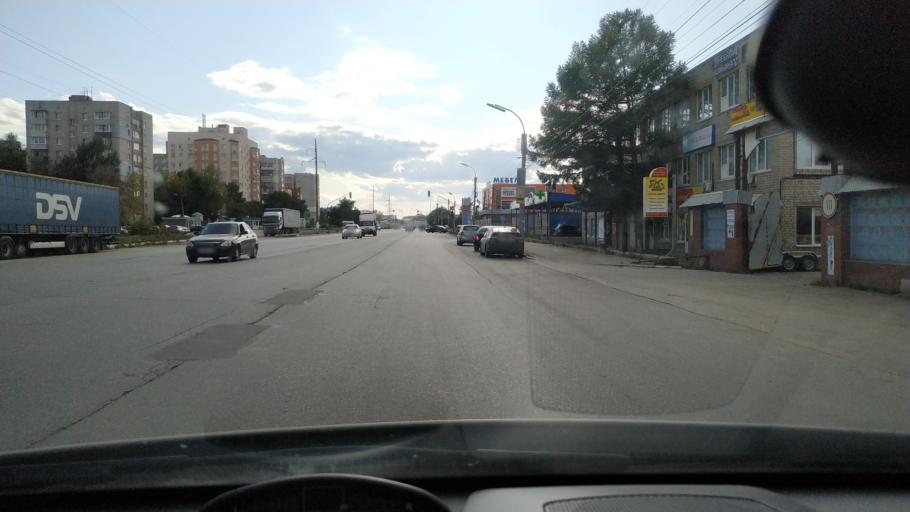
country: RU
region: Rjazan
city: Ryazan'
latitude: 54.6203
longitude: 39.7014
